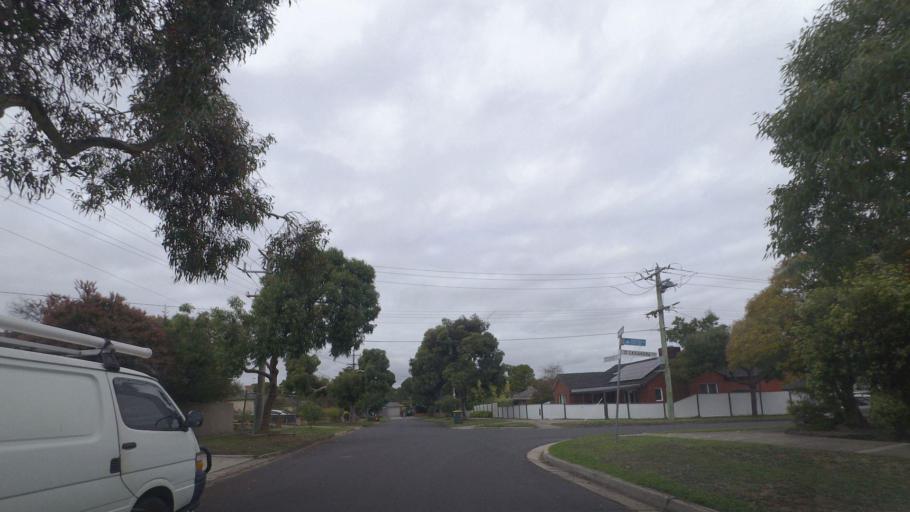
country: AU
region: Victoria
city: Forest Hill
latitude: -37.8296
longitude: 145.1836
